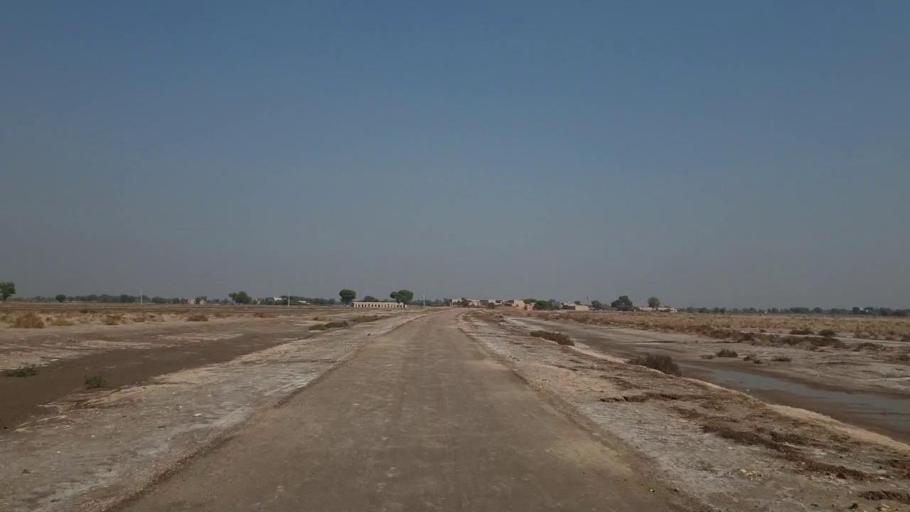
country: PK
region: Sindh
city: Sehwan
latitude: 26.4300
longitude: 67.7714
